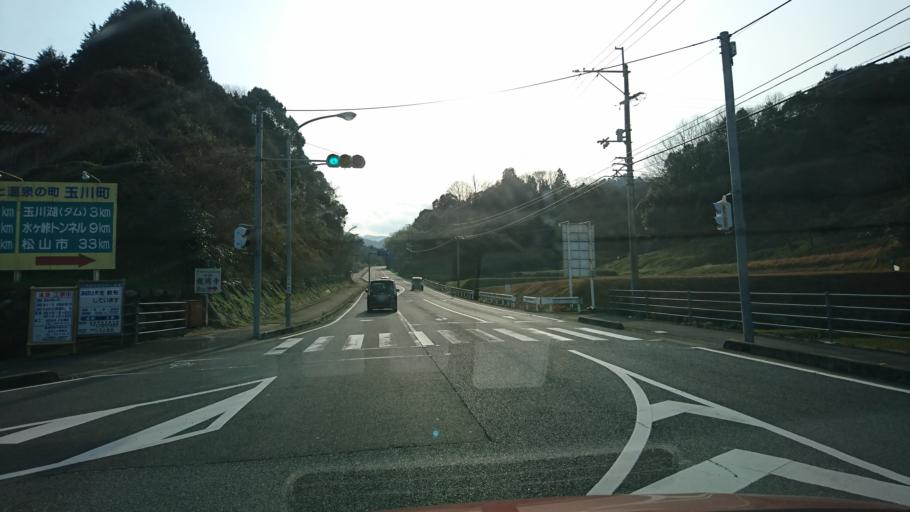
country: JP
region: Ehime
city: Hojo
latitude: 34.0019
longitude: 132.9377
